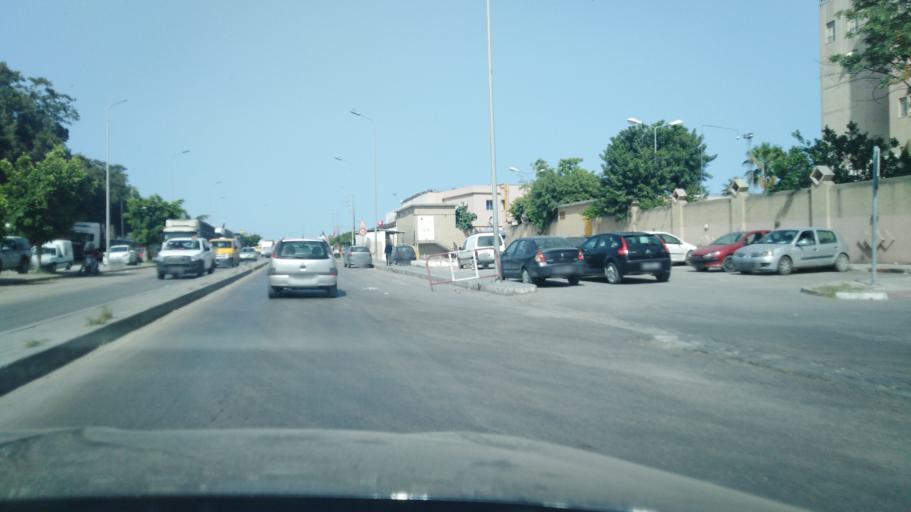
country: TN
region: Susah
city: Sousse
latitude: 35.8121
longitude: 10.6270
